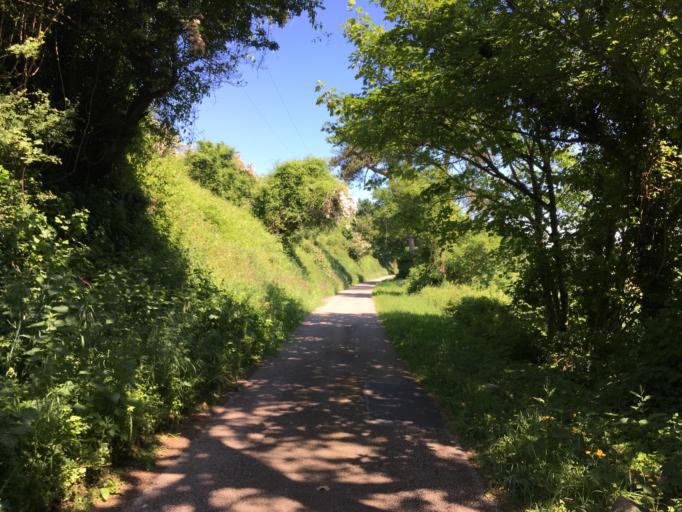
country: GB
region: England
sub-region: Devon
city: Dartmouth
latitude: 50.3441
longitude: -3.5578
